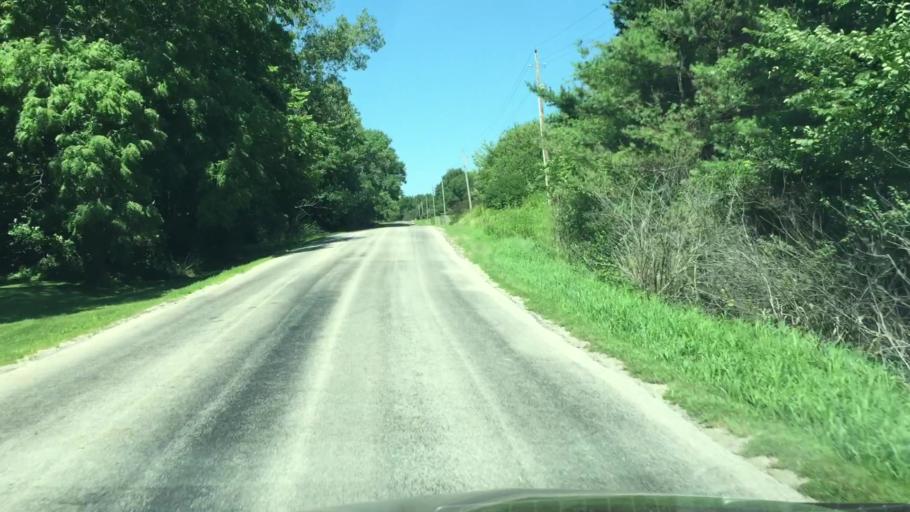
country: US
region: Iowa
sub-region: Linn County
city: Ely
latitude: 41.8150
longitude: -91.6024
